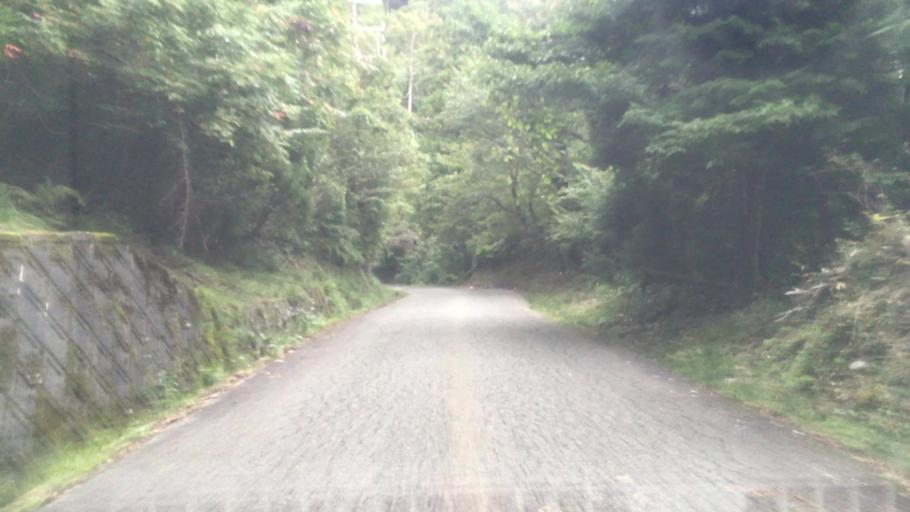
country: JP
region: Hyogo
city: Toyooka
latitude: 35.6208
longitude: 134.8767
